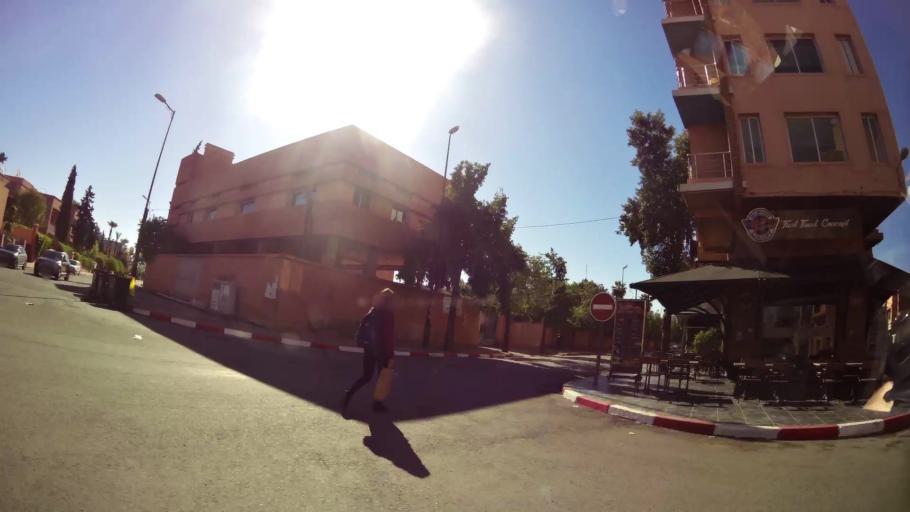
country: MA
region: Marrakech-Tensift-Al Haouz
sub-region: Marrakech
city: Marrakesh
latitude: 31.6423
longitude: -8.0181
